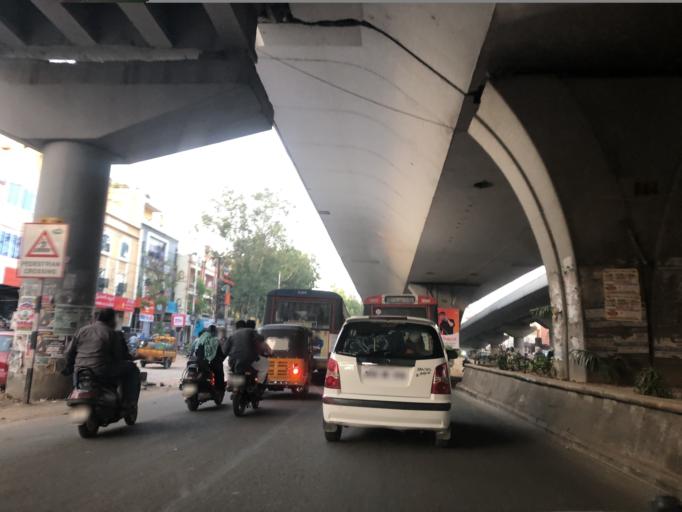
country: IN
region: Telangana
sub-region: Hyderabad
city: Hyderabad
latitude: 17.3824
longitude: 78.4293
